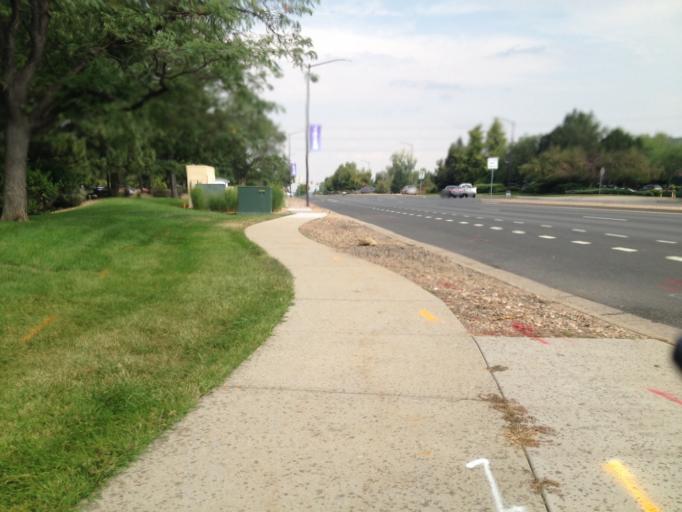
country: US
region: Colorado
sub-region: Boulder County
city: Louisville
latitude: 39.9870
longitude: -105.1584
